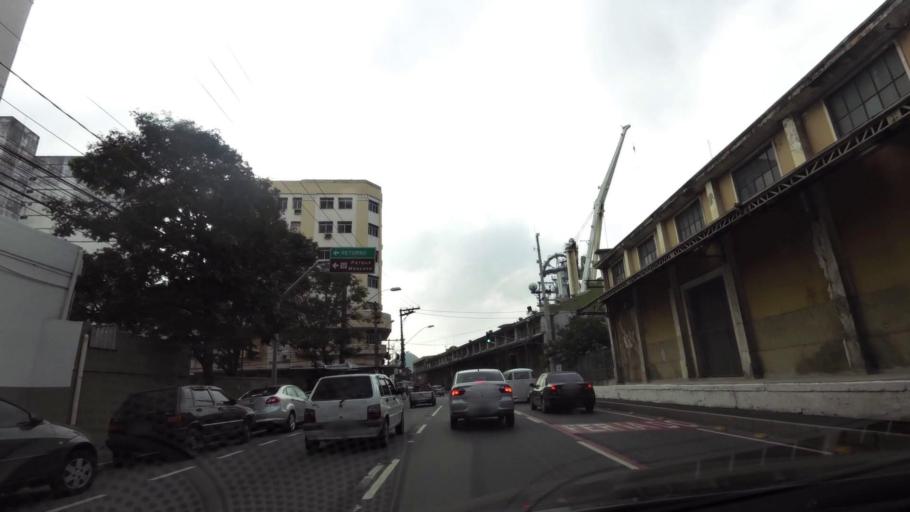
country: BR
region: Espirito Santo
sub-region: Vitoria
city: Vitoria
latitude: -20.3220
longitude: -40.3419
